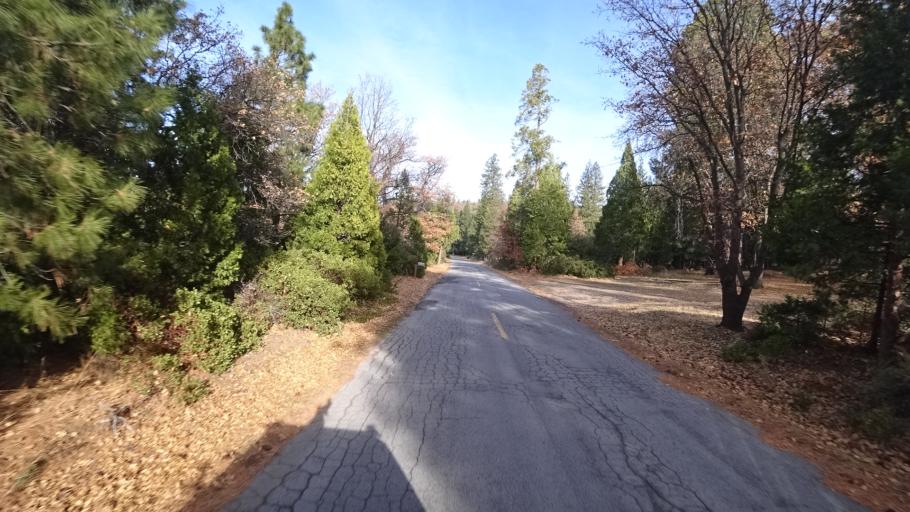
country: US
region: California
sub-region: Siskiyou County
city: Weed
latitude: 41.4458
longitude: -122.3814
